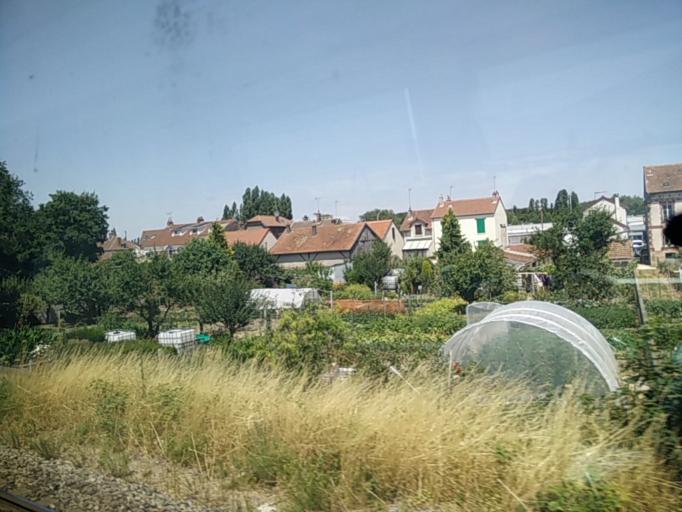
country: FR
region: Ile-de-France
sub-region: Departement de Seine-et-Marne
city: Nangis
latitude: 48.5604
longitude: 3.0144
